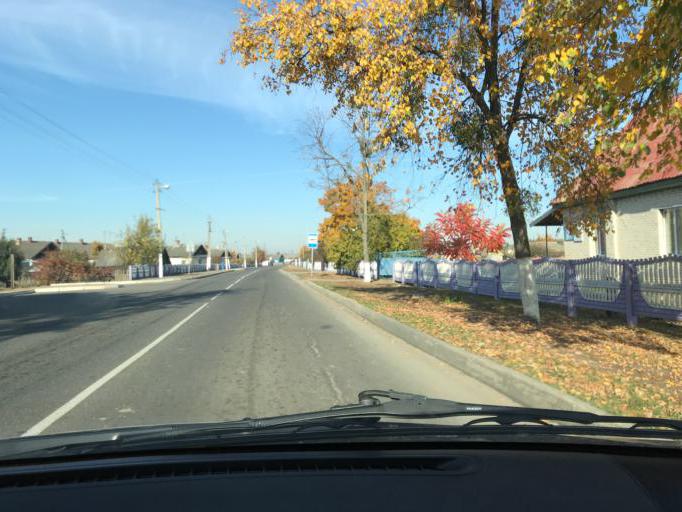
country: BY
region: Brest
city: Mikashevichy
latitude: 52.2232
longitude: 27.4640
